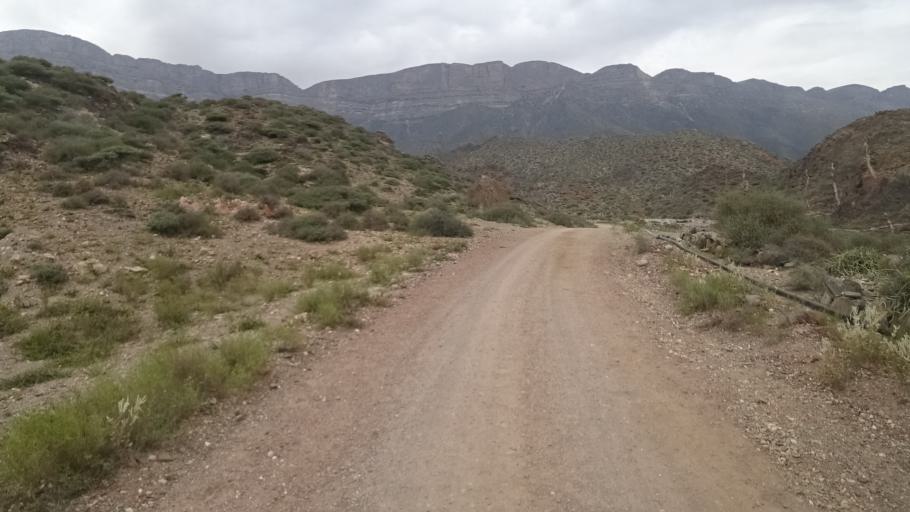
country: OM
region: Zufar
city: Salalah
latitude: 17.1739
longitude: 54.9505
